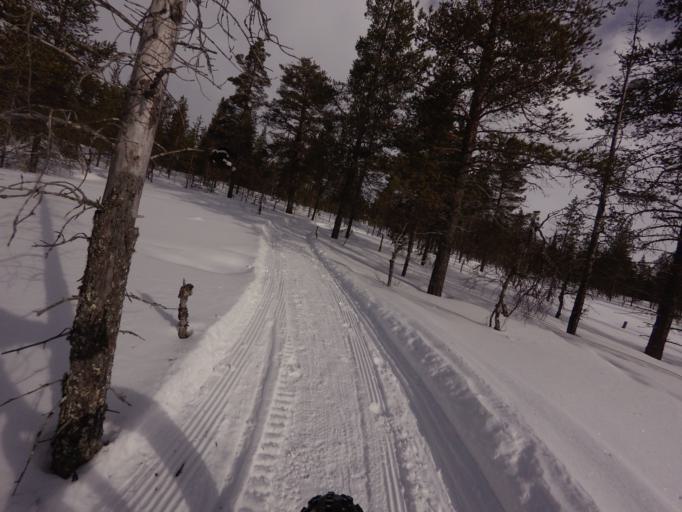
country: FI
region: Lapland
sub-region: Pohjois-Lappi
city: Ivalo
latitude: 68.3449
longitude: 27.4427
